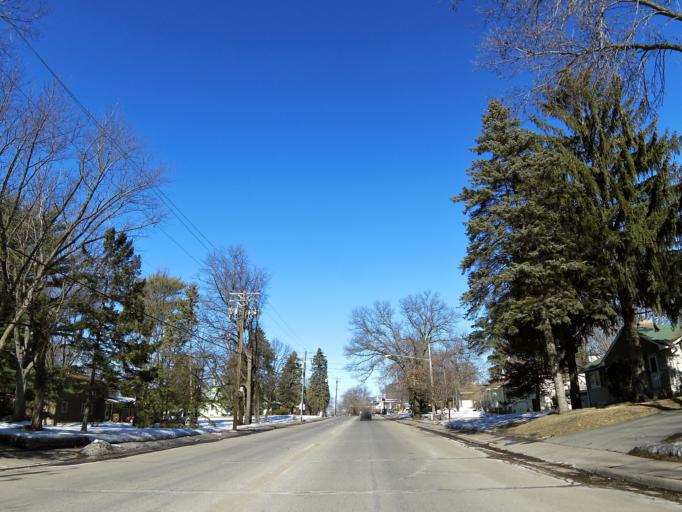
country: US
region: Minnesota
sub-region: Washington County
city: Stillwater
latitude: 45.0633
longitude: -92.8205
